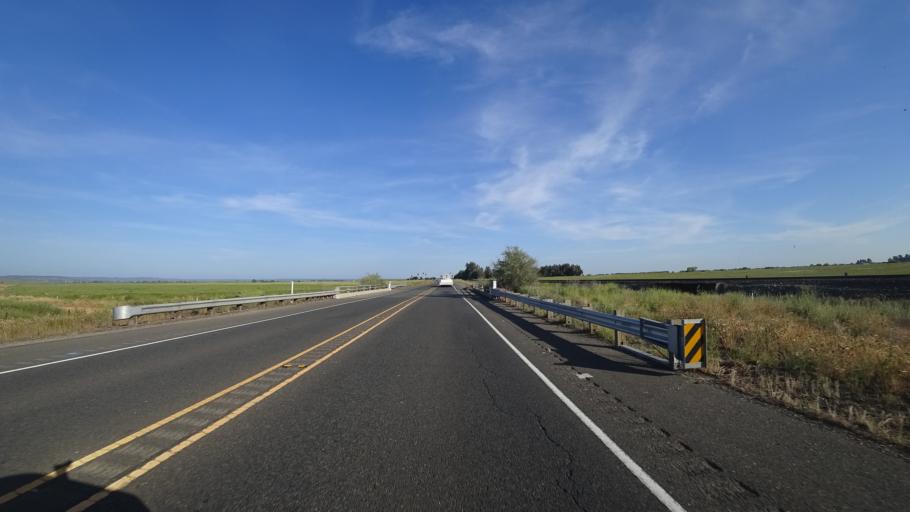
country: US
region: California
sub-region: Placer County
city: Sheridan
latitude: 38.9698
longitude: -121.3672
